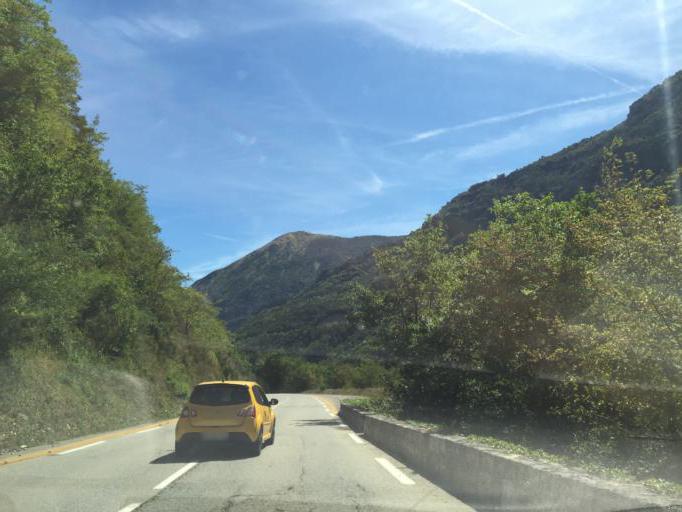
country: FR
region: Provence-Alpes-Cote d'Azur
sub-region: Departement des Alpes-Maritimes
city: Saint-Martin-Vesubie
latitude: 43.9950
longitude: 7.1370
